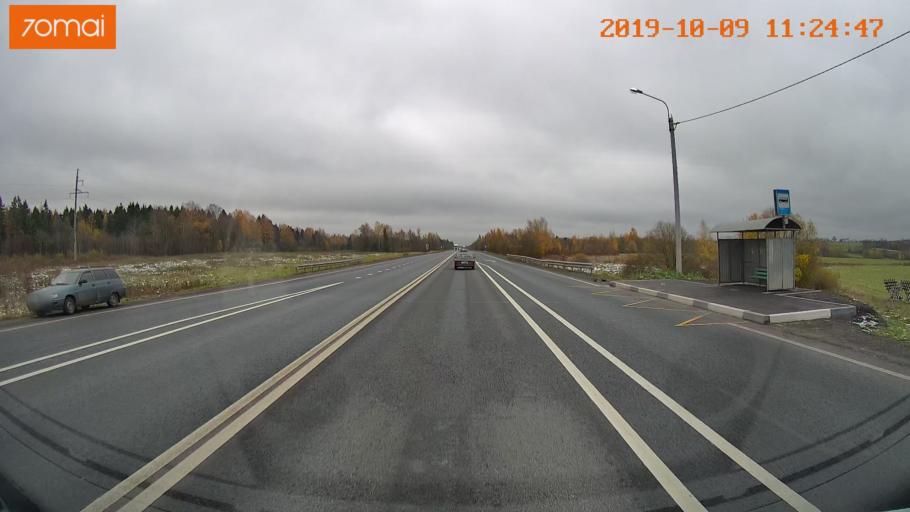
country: RU
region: Vologda
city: Vologda
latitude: 59.1081
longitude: 39.9837
